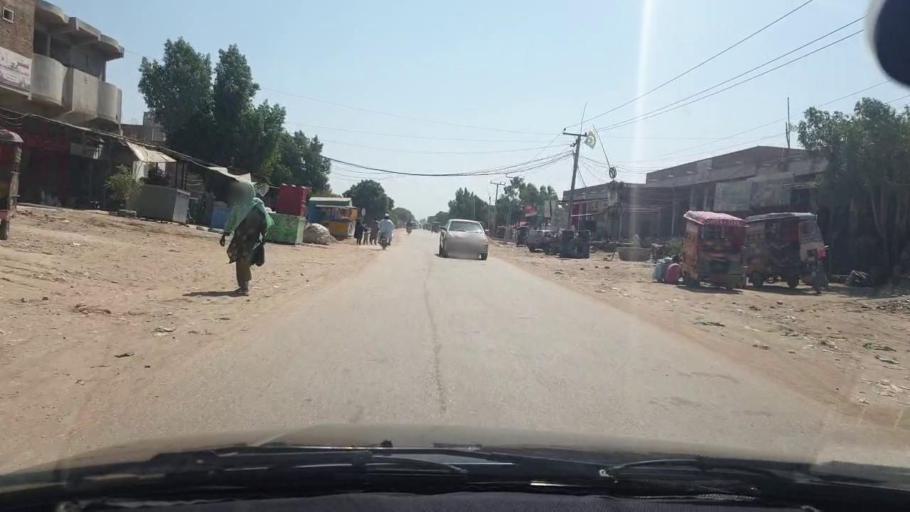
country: PK
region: Sindh
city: Tando Allahyar
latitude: 25.4514
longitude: 68.7253
